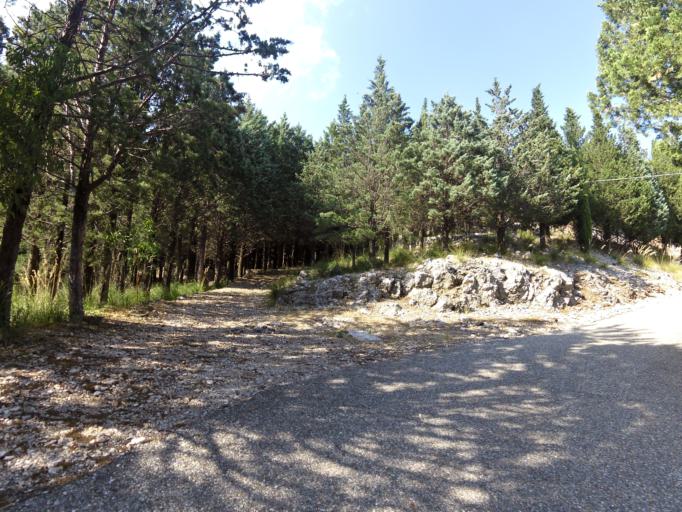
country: IT
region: Calabria
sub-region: Provincia di Reggio Calabria
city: Pazzano
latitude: 38.4685
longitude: 16.4485
